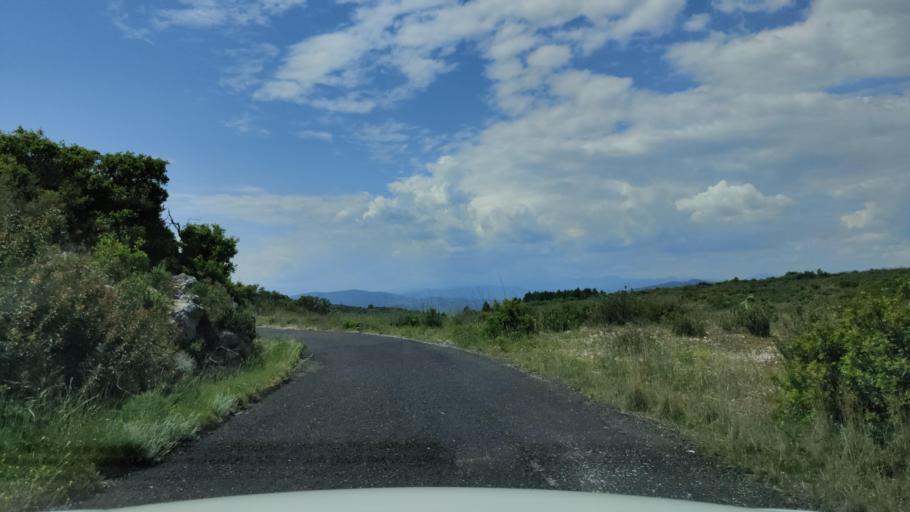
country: FR
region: Languedoc-Roussillon
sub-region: Departement des Pyrenees-Orientales
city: Estagel
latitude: 42.7920
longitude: 2.7330
